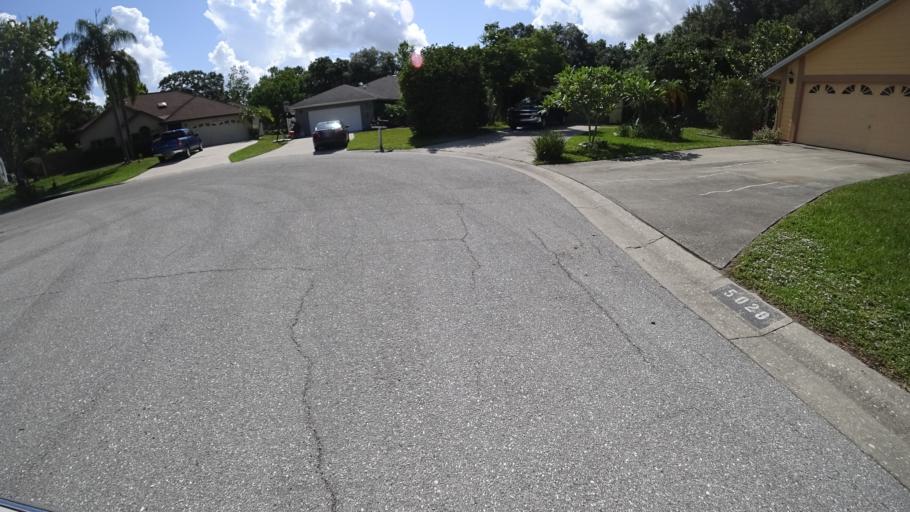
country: US
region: Florida
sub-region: Sarasota County
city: Desoto Lakes
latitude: 27.3952
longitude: -82.4980
